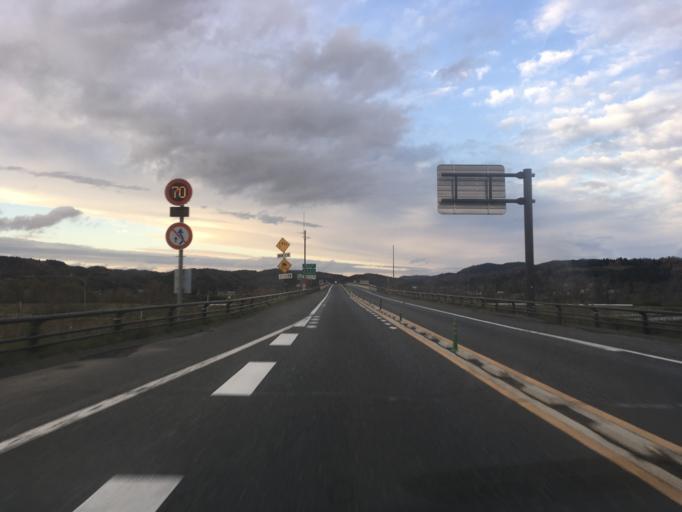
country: JP
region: Miyagi
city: Wakuya
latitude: 38.6010
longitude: 141.2827
